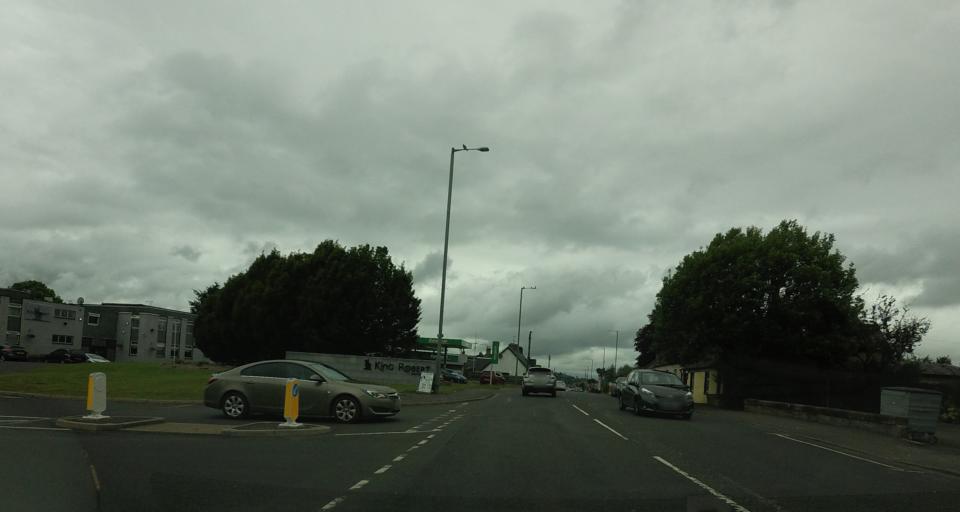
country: GB
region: Scotland
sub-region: Stirling
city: Bannockburn
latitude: 56.0929
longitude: -3.9334
